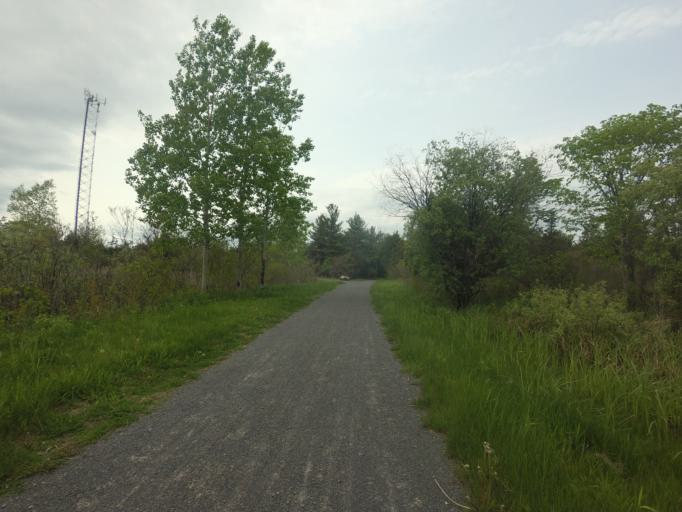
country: CA
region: Ontario
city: Kingston
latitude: 44.2811
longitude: -76.5631
